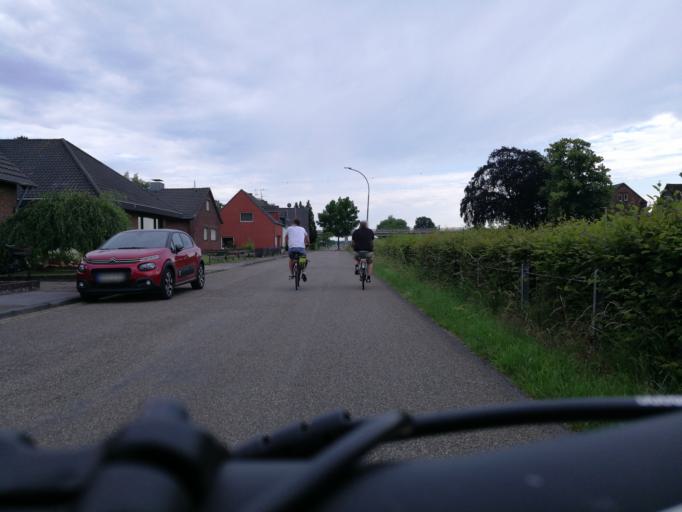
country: DE
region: North Rhine-Westphalia
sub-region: Regierungsbezirk Dusseldorf
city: Kleve
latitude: 51.8205
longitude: 6.1418
